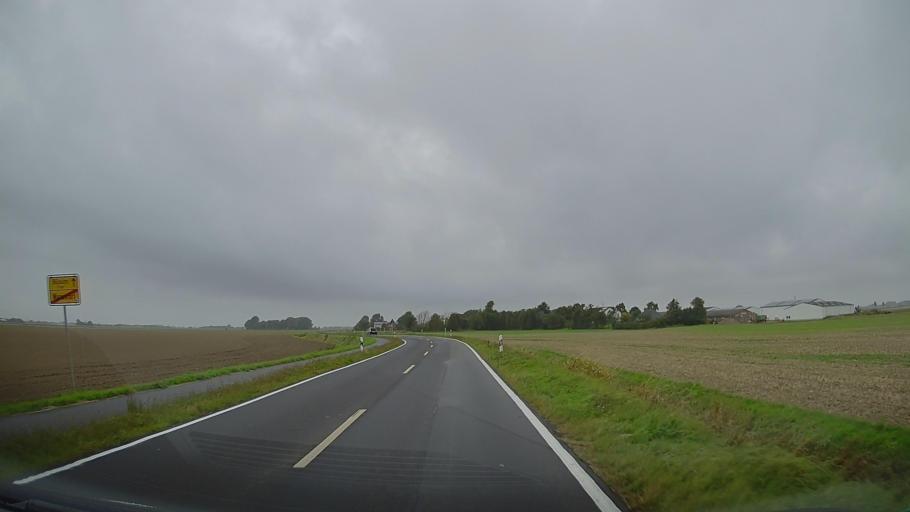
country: DE
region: Schleswig-Holstein
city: Wesselburener Deichhausen
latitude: 54.1431
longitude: 8.9226
